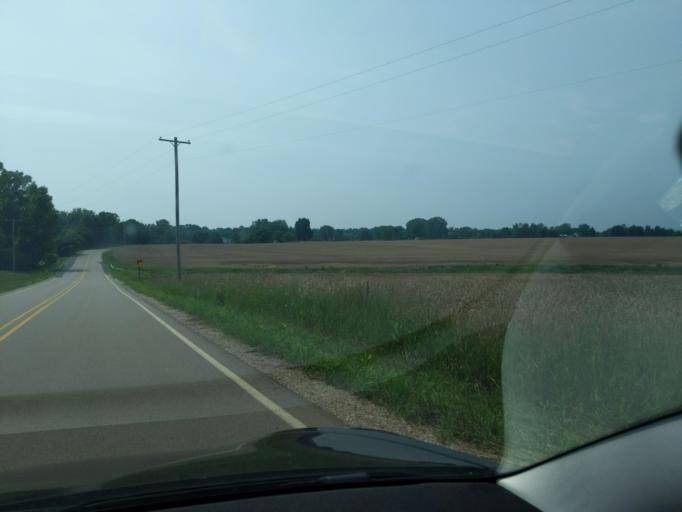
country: US
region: Michigan
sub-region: Clinton County
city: DeWitt
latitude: 42.9148
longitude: -84.5784
